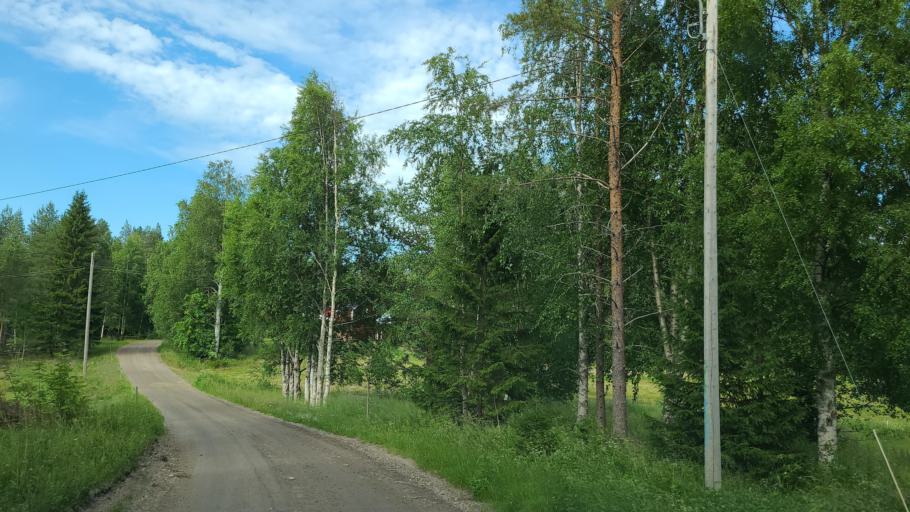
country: SE
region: Vaesterbotten
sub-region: Robertsfors Kommun
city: Robertsfors
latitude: 64.1548
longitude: 20.9238
